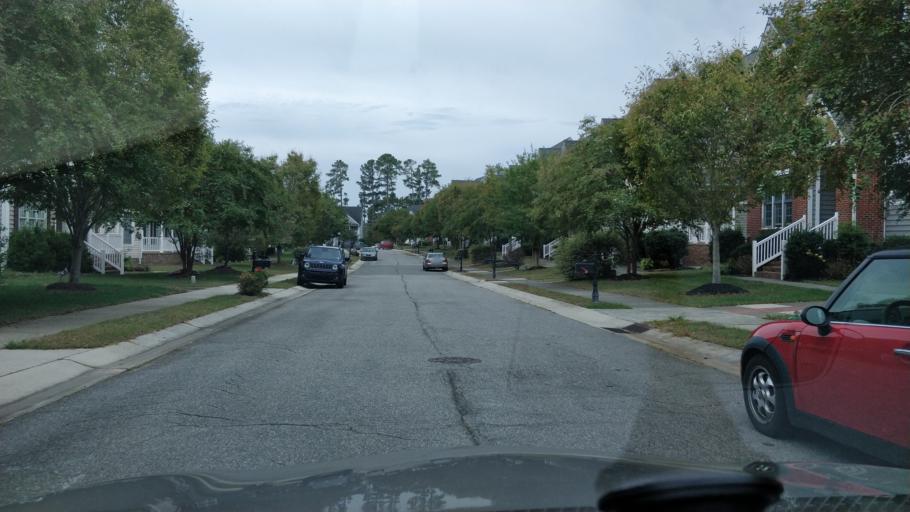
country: US
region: North Carolina
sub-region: Wake County
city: Morrisville
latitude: 35.8211
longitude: -78.8359
